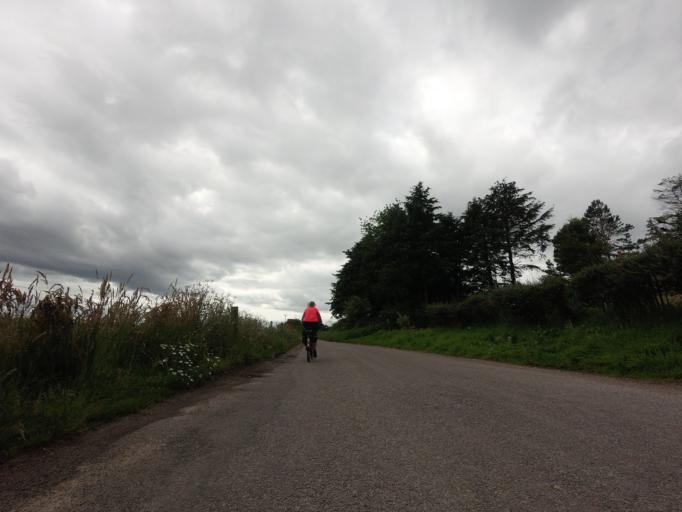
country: GB
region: Scotland
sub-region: Moray
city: Forres
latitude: 57.6094
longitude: -3.6899
